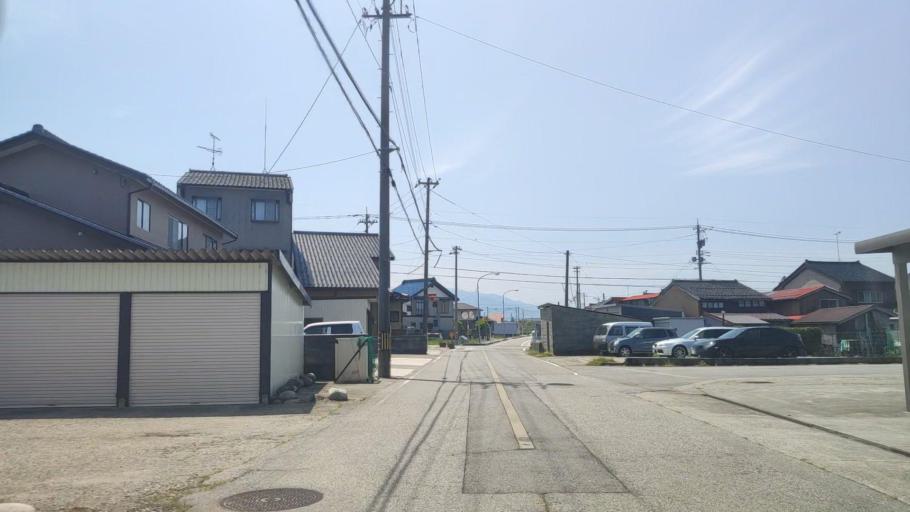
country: JP
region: Toyama
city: Nyuzen
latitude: 36.9580
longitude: 137.5679
